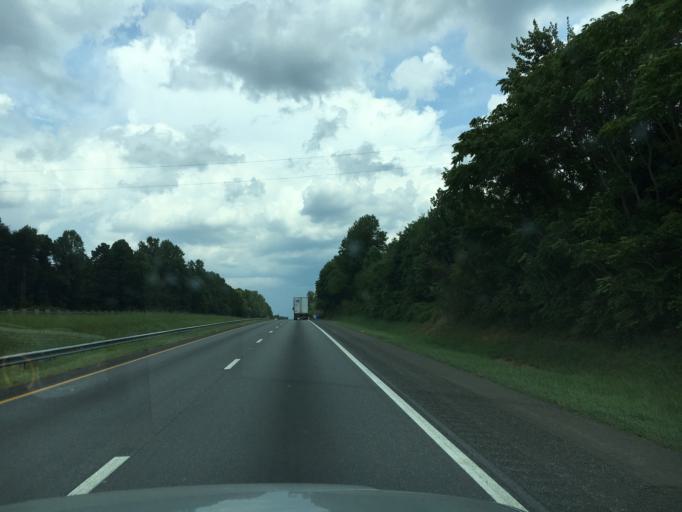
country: US
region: North Carolina
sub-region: Cleveland County
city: Kings Mountain
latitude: 35.2147
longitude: -81.3479
